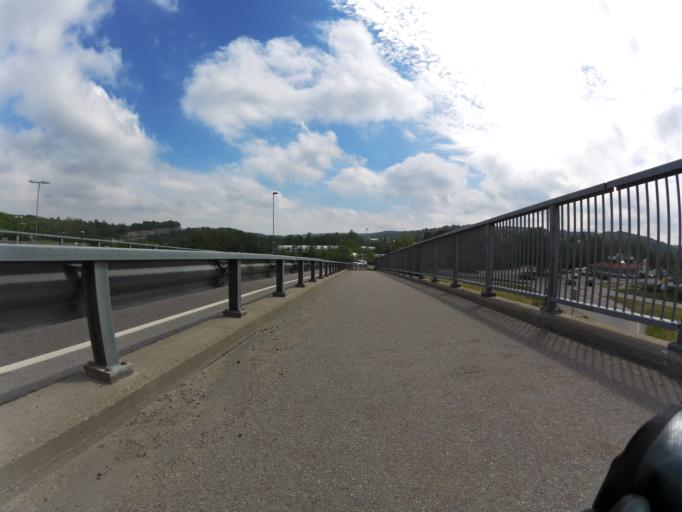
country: NO
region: Ostfold
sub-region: Rade
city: Karlshus
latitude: 59.3254
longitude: 10.9565
